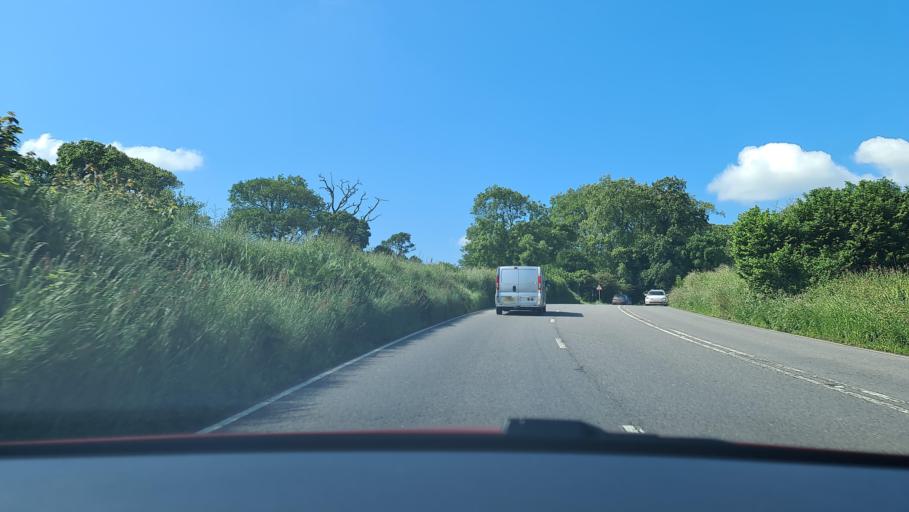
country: GB
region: England
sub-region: Cornwall
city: Lostwithiel
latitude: 50.4022
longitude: -4.6834
